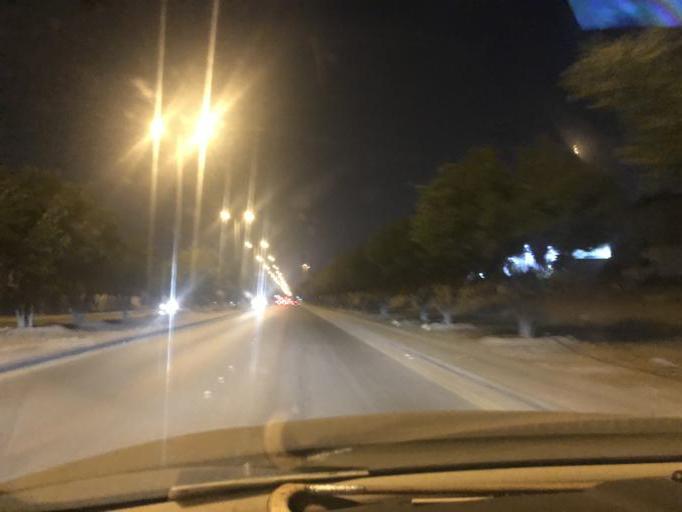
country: SA
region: Ar Riyad
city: Riyadh
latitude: 24.6794
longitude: 46.7907
